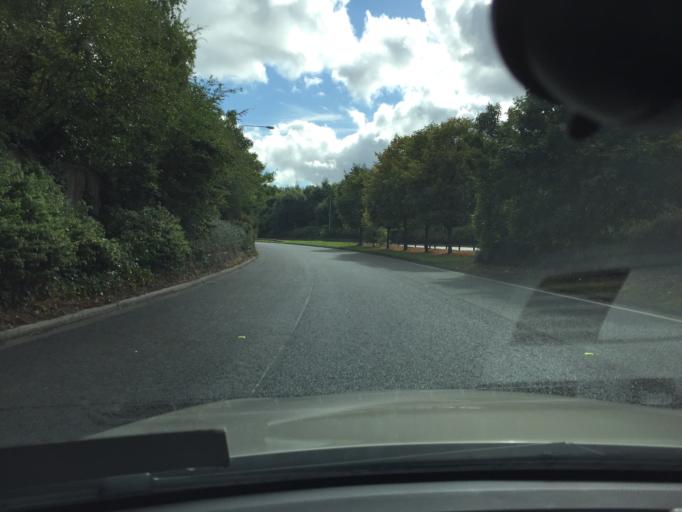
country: IE
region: Leinster
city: Chapelizod
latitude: 53.3458
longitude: -6.3465
